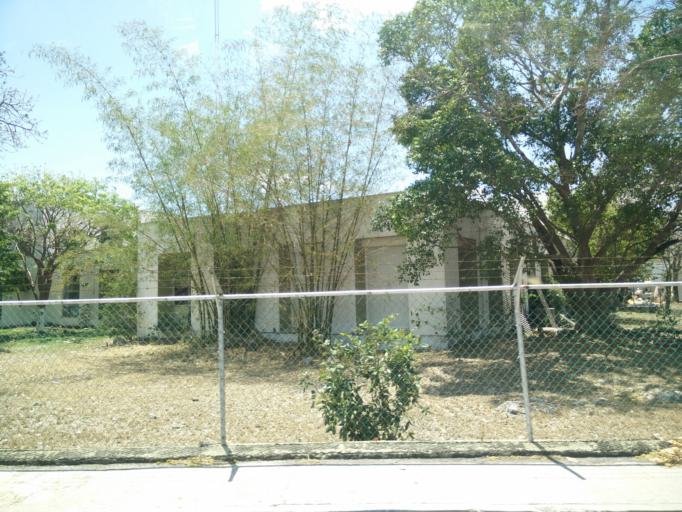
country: MX
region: Yucatan
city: Merida
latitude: 21.0269
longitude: -89.6250
